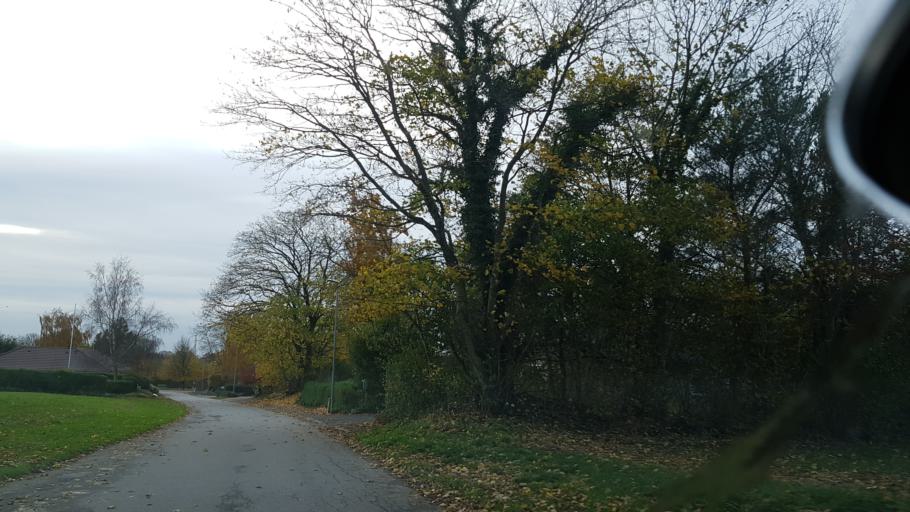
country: DK
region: South Denmark
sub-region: Haderslev Kommune
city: Vojens
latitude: 55.3027
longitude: 9.3792
